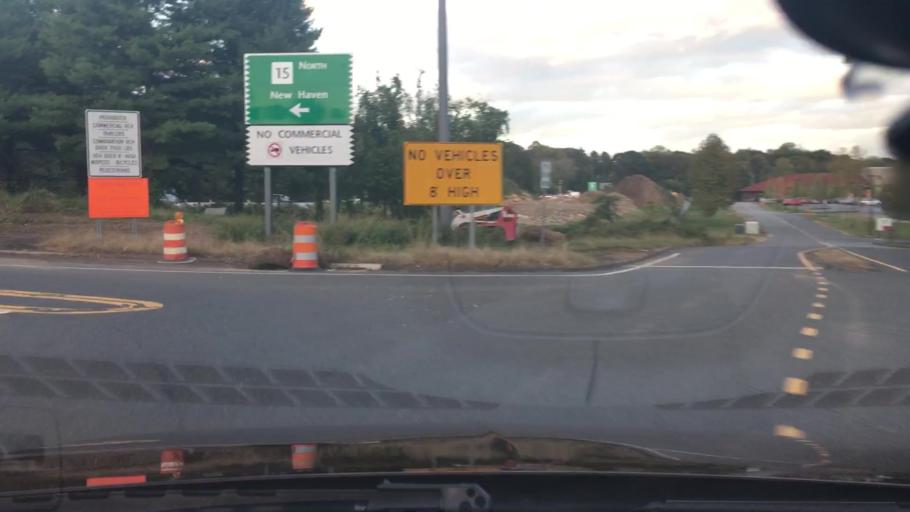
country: US
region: Connecticut
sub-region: Fairfield County
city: Westport
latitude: 41.1632
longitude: -73.3731
